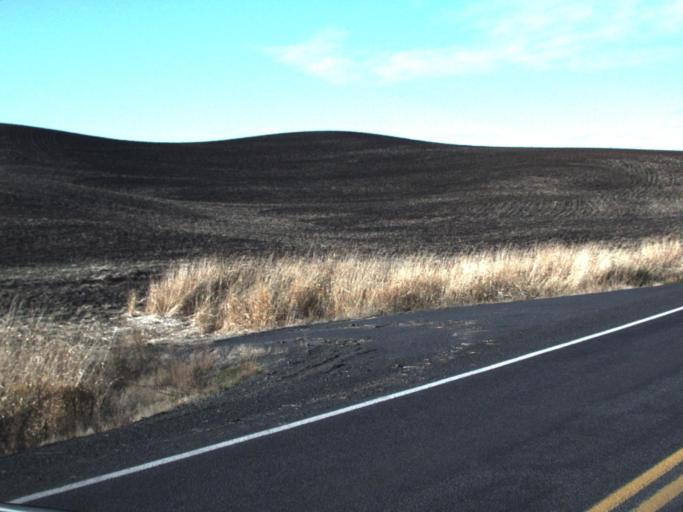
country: US
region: Washington
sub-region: Whitman County
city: Pullman
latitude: 46.7260
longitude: -117.2243
